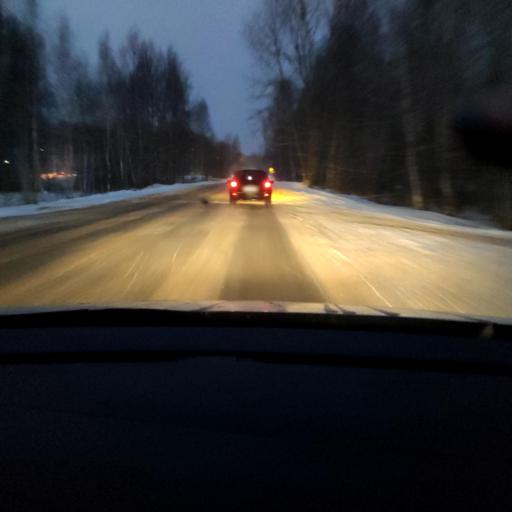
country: RU
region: Tatarstan
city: Aysha
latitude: 55.8696
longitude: 48.5801
